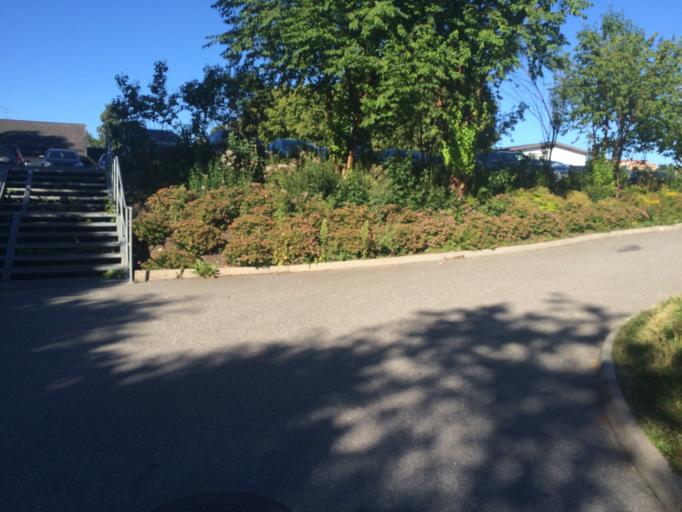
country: SE
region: Stockholm
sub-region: Sollentuna Kommun
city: Sollentuna
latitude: 59.4443
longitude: 17.9319
